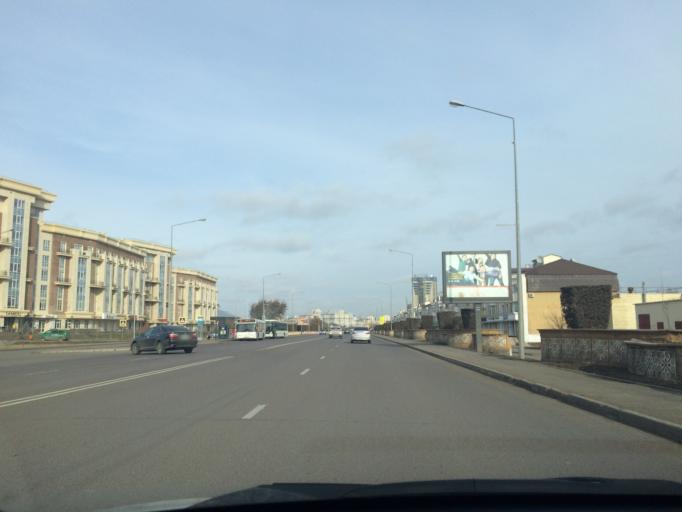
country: KZ
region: Astana Qalasy
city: Astana
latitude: 51.1398
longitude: 71.4180
